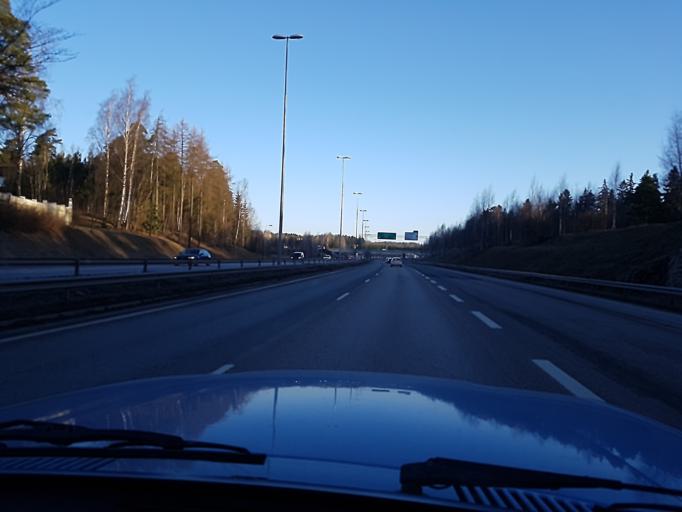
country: FI
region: Uusimaa
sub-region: Helsinki
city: Helsinki
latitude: 60.2253
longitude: 24.9450
